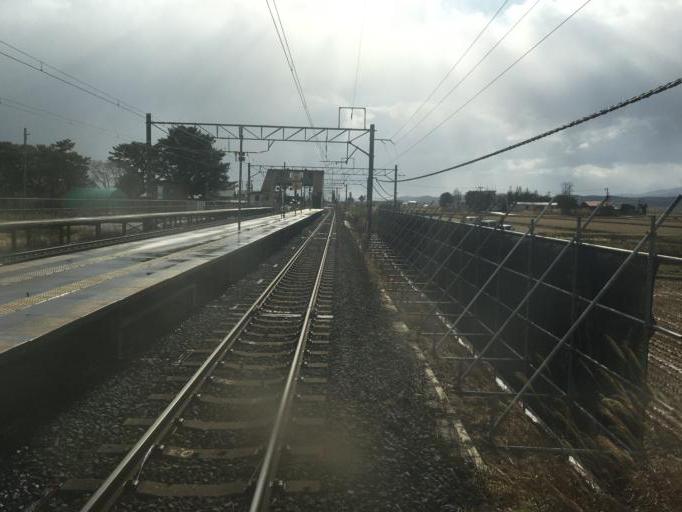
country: JP
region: Aomori
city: Aomori Shi
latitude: 40.9502
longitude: 140.6560
